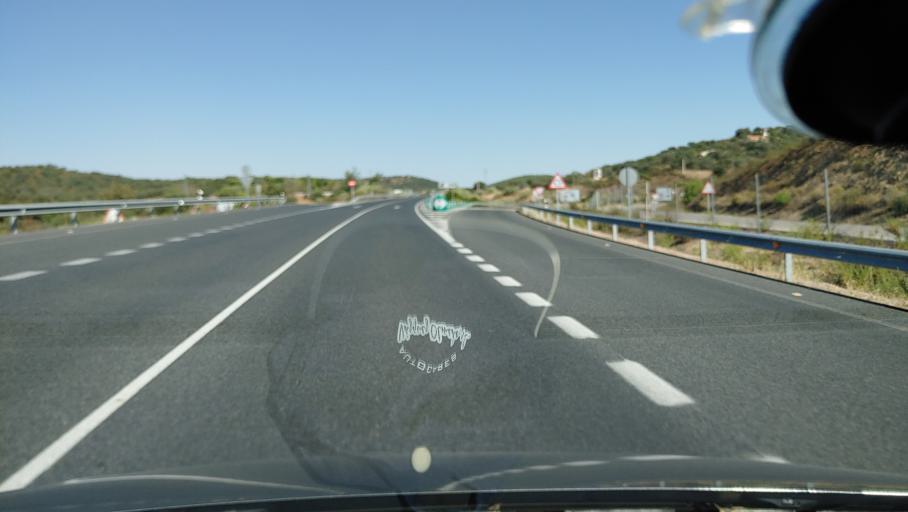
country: ES
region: Andalusia
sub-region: Province of Cordoba
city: Villaharta
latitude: 38.0943
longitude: -4.8685
